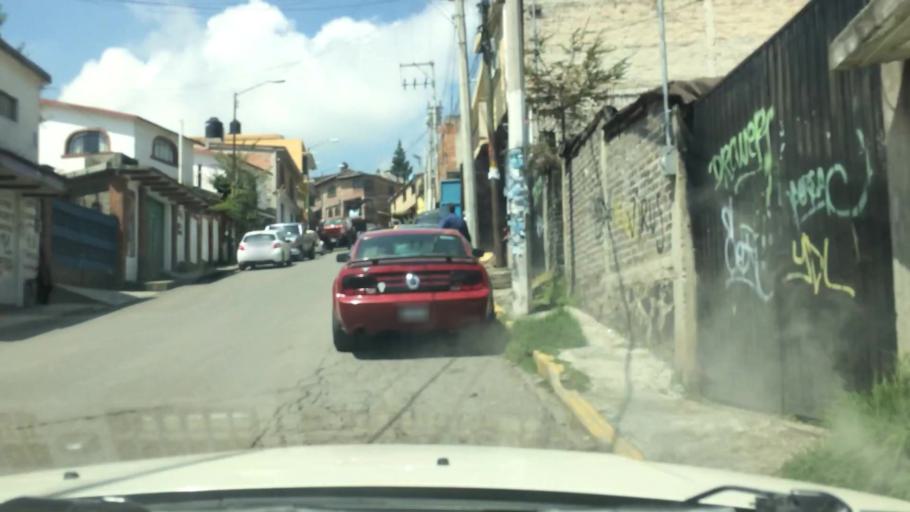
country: MX
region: Mexico City
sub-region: Tlalpan
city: Lomas de Tepemecatl
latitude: 19.2259
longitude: -99.2036
